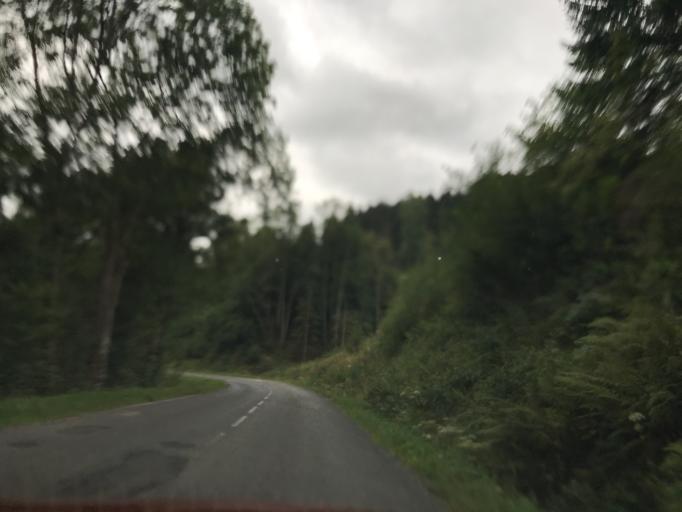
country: FR
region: Rhone-Alpes
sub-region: Departement de la Loire
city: Sail-sous-Couzan
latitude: 45.6958
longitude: 3.8546
